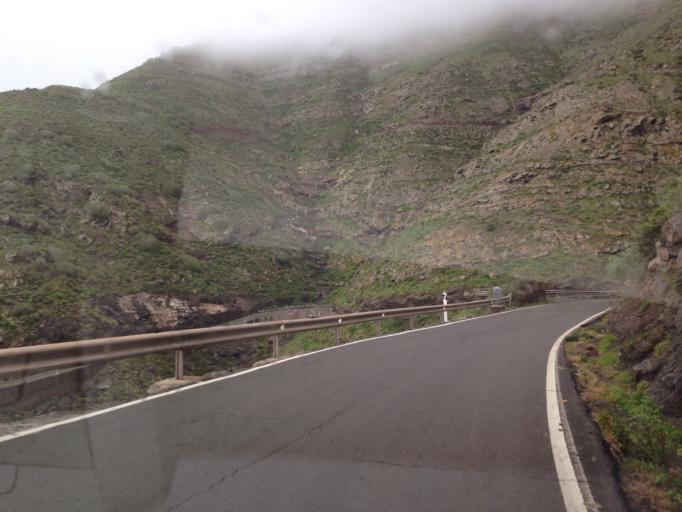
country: ES
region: Canary Islands
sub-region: Provincia de Las Palmas
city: San Nicolas
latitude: 28.0352
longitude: -15.7561
